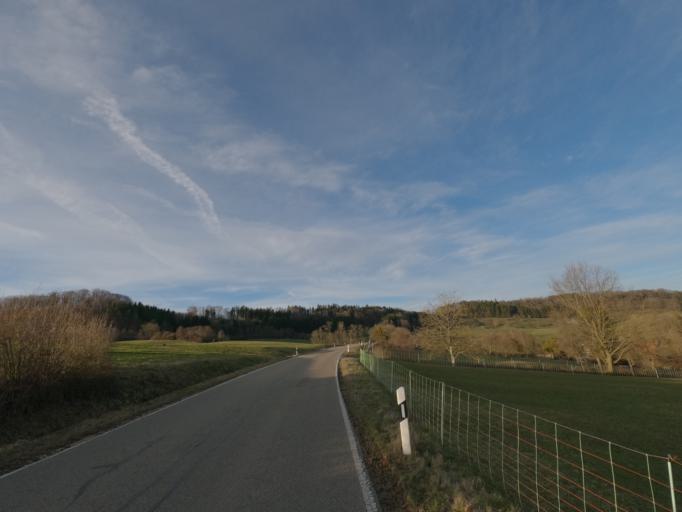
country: DE
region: Baden-Wuerttemberg
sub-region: Regierungsbezirk Stuttgart
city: Ottenbach
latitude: 48.7440
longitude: 9.7515
